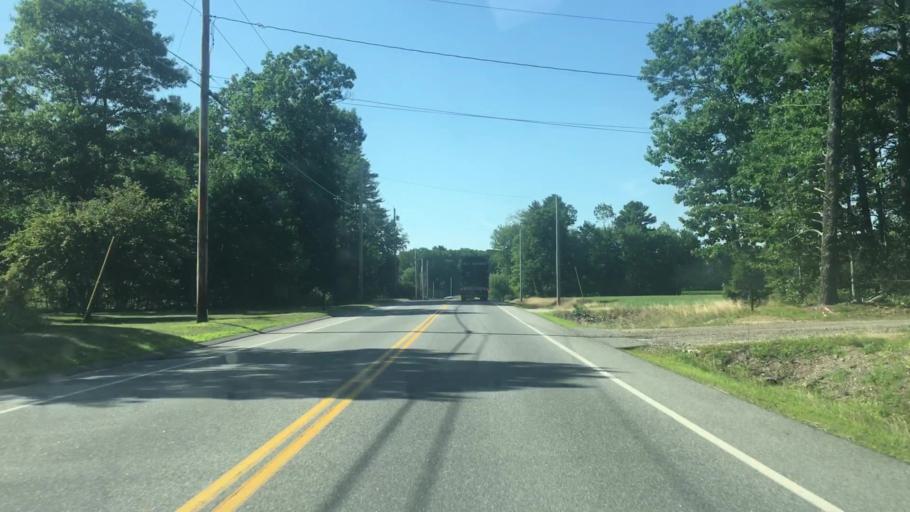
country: US
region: Maine
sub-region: York County
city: Buxton
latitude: 43.5921
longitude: -70.5260
